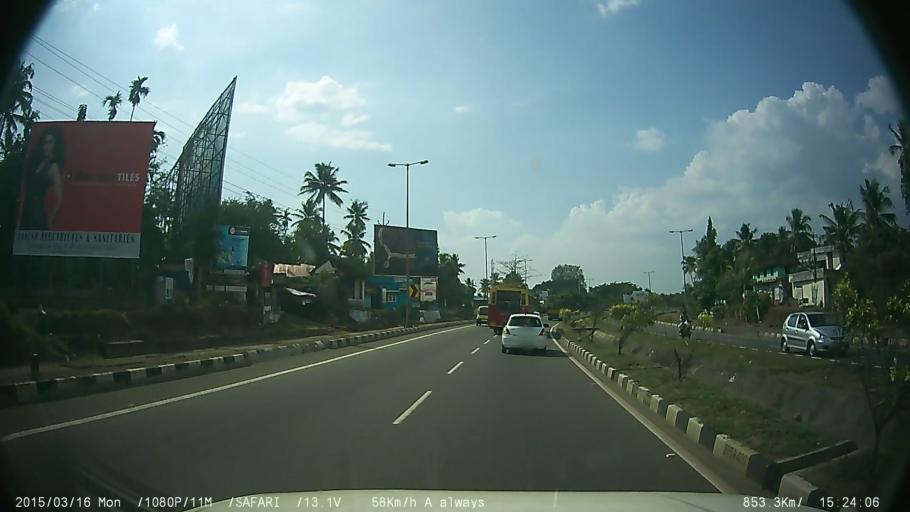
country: IN
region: Kerala
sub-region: Thrissur District
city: Irinjalakuda
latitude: 10.3853
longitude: 76.2903
